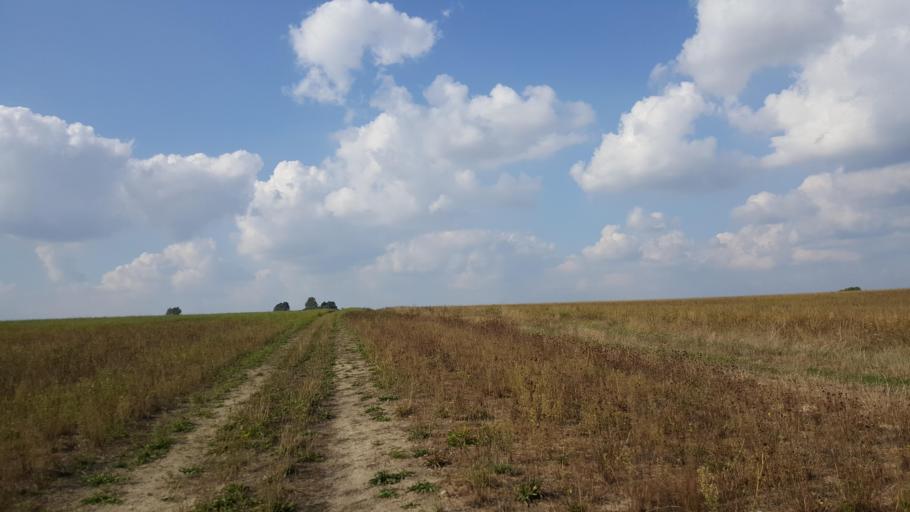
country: BY
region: Brest
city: Kamyanyets
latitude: 52.4191
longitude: 23.8149
